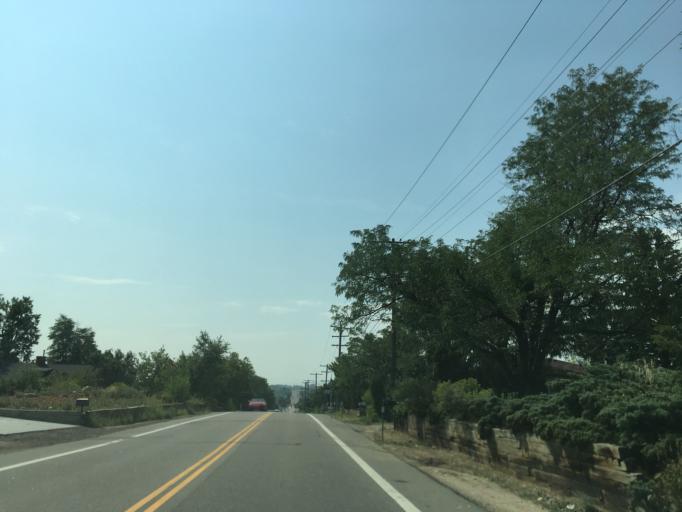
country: US
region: Colorado
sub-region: Jefferson County
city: Applewood
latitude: 39.7450
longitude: -105.1282
